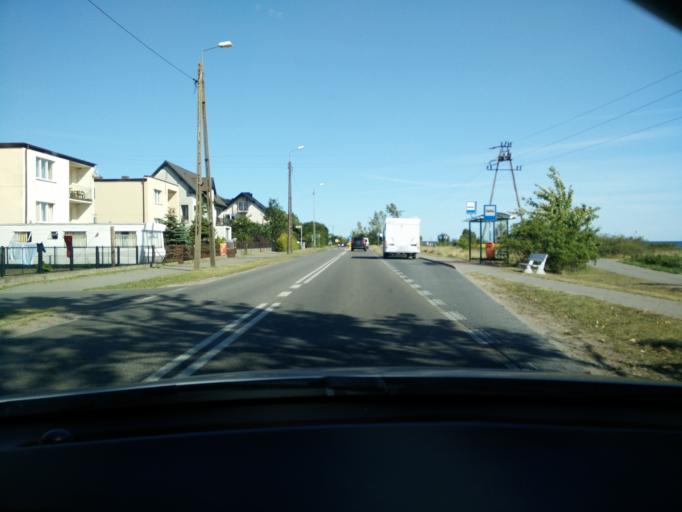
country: PL
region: Pomeranian Voivodeship
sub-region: Powiat pucki
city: Jastarnia
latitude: 54.7285
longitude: 18.5969
